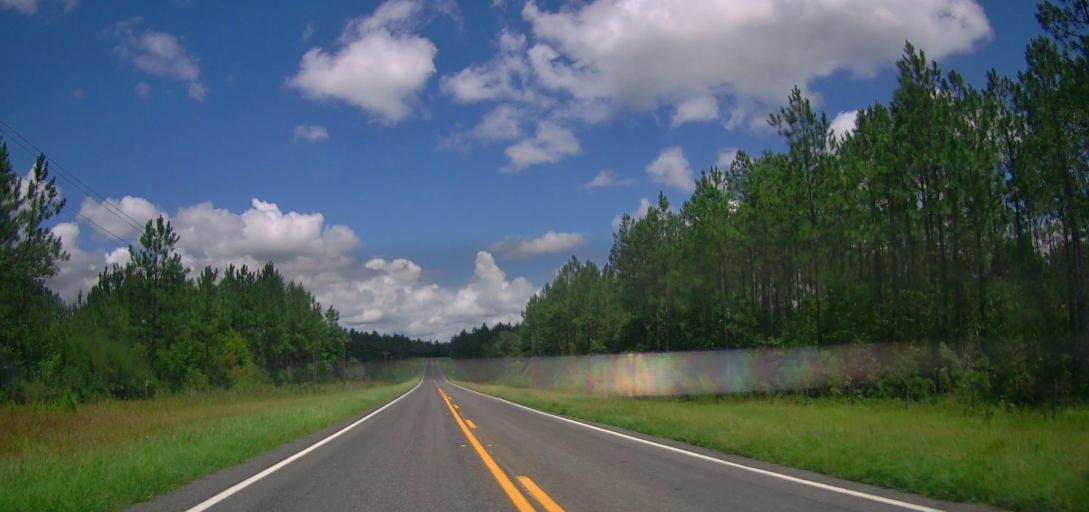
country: US
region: Georgia
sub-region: Turner County
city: Ashburn
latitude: 31.7518
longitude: -83.6427
